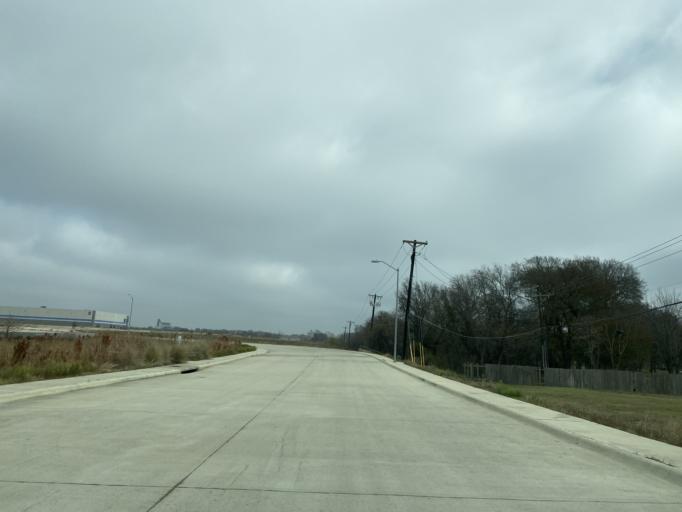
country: US
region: Texas
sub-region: Williamson County
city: Round Rock
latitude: 30.5383
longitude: -97.6851
